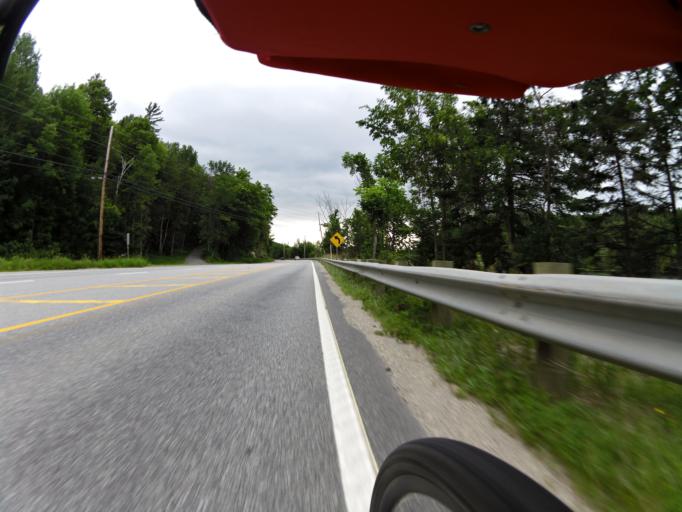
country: CA
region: Quebec
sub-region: Outaouais
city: Wakefield
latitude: 45.6741
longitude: -75.9290
